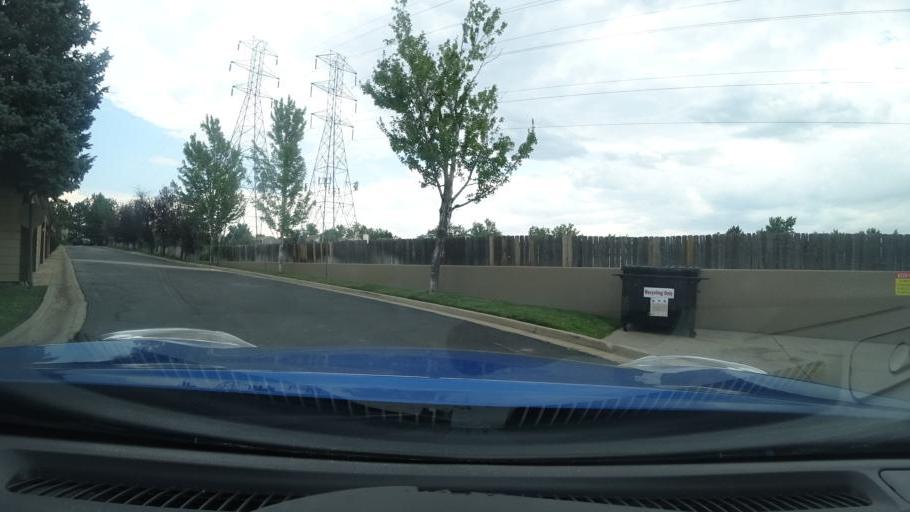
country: US
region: Colorado
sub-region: Adams County
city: Aurora
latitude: 39.6826
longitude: -104.7888
